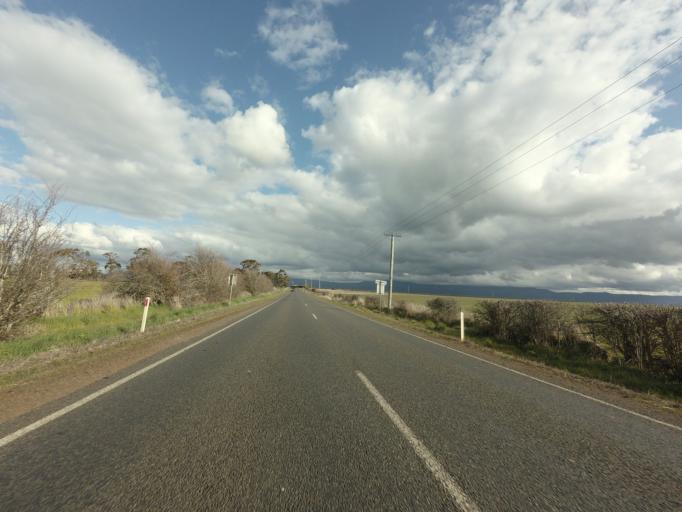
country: AU
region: Tasmania
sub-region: Northern Midlands
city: Longford
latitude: -41.6991
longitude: 147.0774
